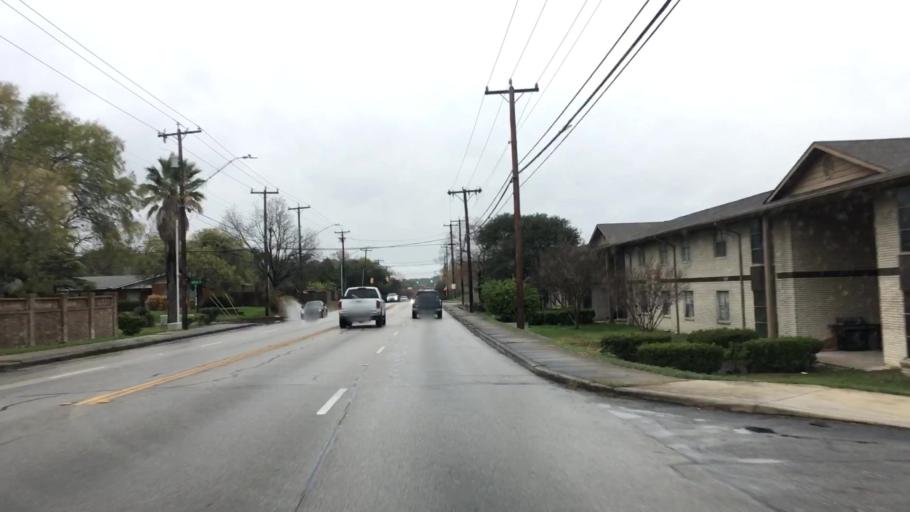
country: US
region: Texas
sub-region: Bexar County
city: Castle Hills
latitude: 29.5107
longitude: -98.5068
